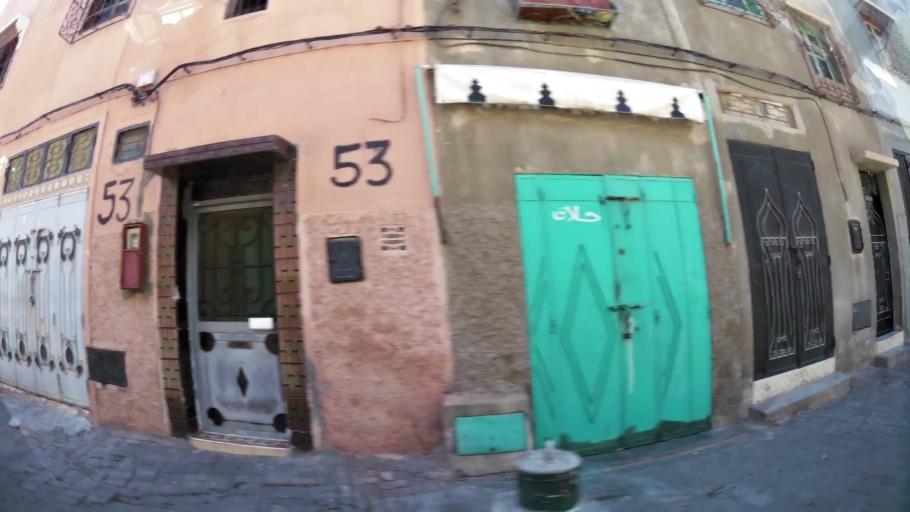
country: MA
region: Marrakech-Tensift-Al Haouz
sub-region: Marrakech
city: Marrakesh
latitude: 31.6376
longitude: -8.0453
